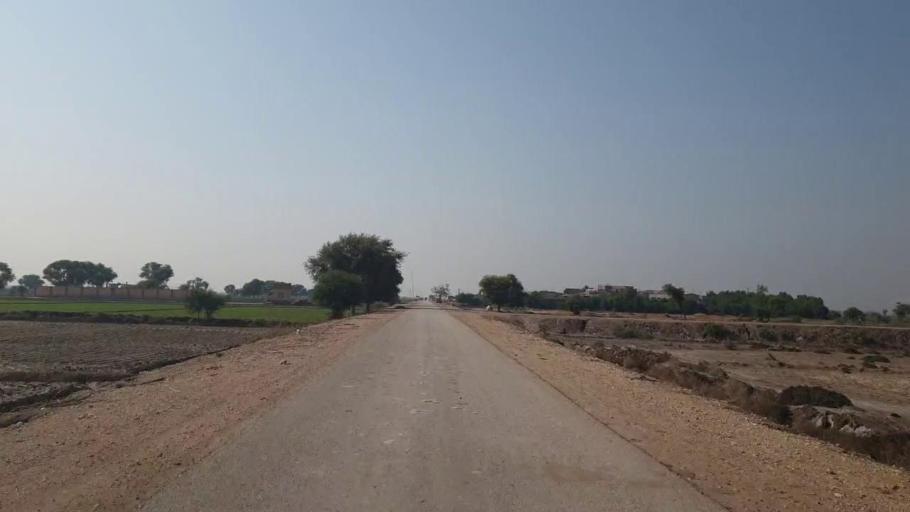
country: PK
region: Sindh
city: Sehwan
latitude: 26.4247
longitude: 67.8316
